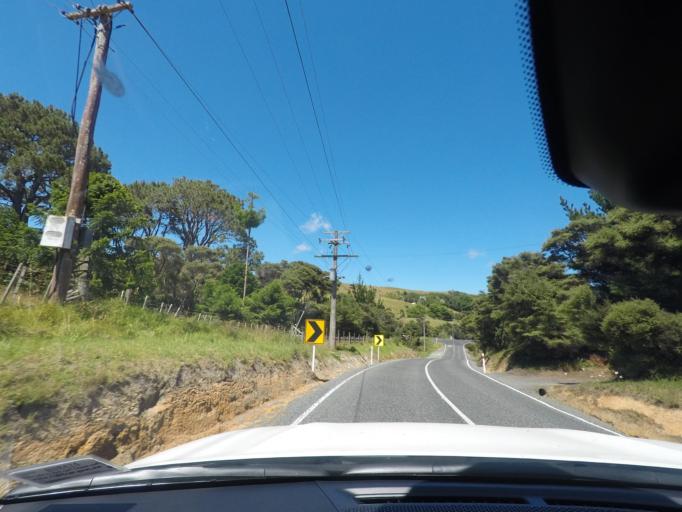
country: NZ
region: Auckland
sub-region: Auckland
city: Parakai
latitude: -36.5833
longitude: 174.3324
